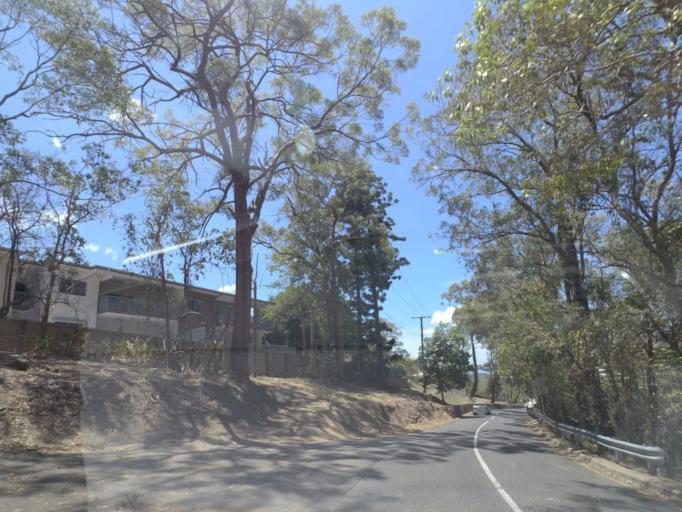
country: AU
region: Queensland
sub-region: Brisbane
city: Mount Gravatt East
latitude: -27.5384
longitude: 153.0756
